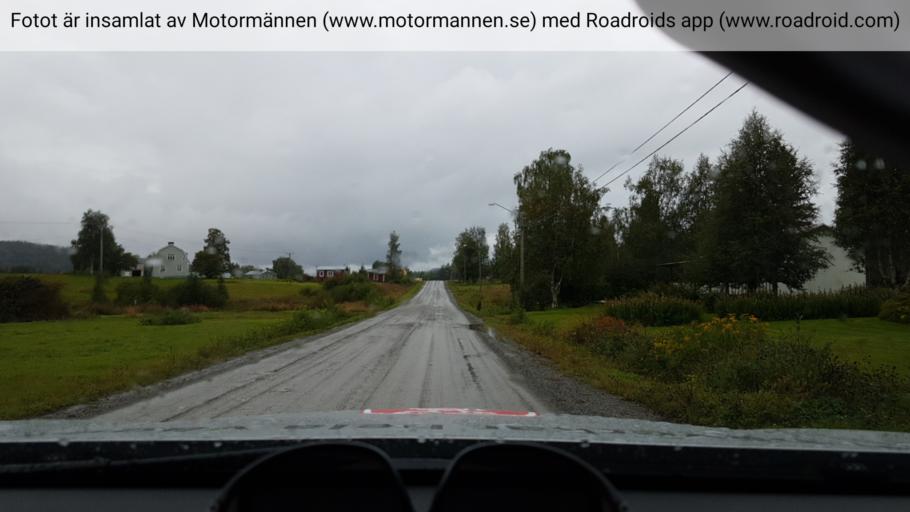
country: SE
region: Vaesterbotten
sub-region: Lycksele Kommun
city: Soderfors
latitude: 64.9671
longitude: 17.6163
